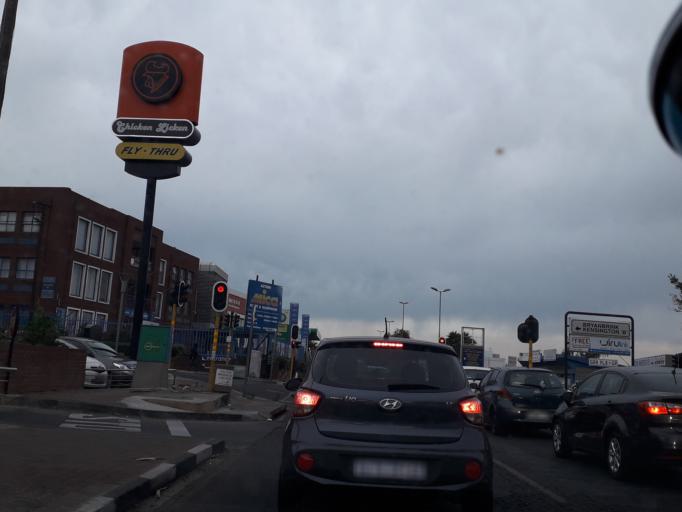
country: ZA
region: Gauteng
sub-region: City of Johannesburg Metropolitan Municipality
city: Johannesburg
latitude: -26.0820
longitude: 28.0090
